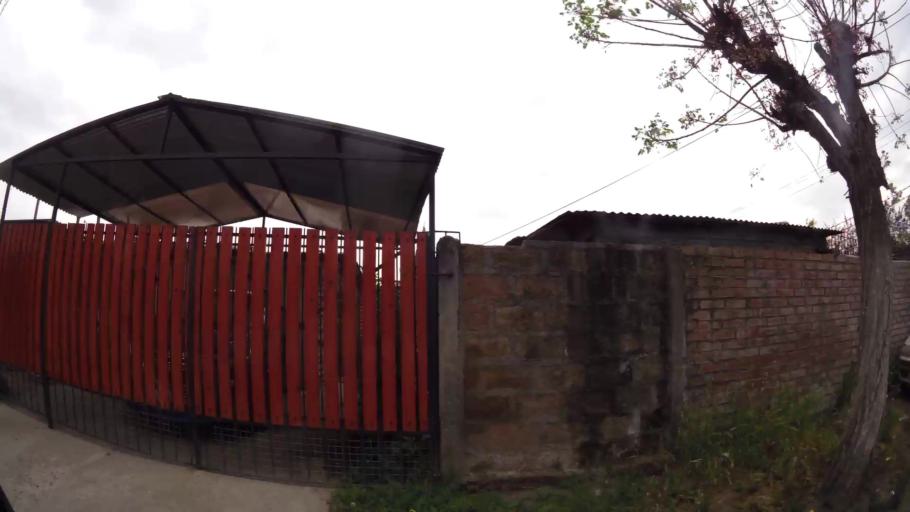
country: CL
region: Santiago Metropolitan
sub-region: Provincia de Santiago
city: Lo Prado
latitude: -33.4967
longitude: -70.7664
